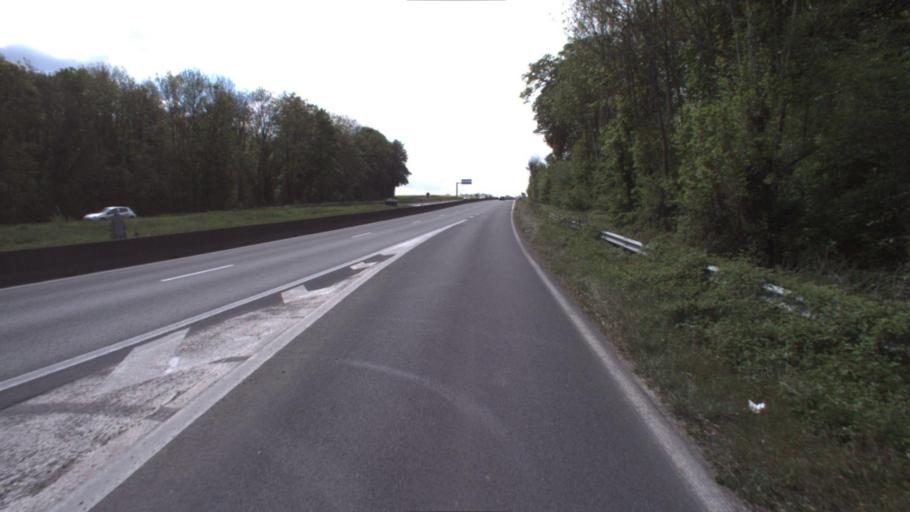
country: FR
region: Ile-de-France
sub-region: Departement de Seine-et-Marne
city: Tournan-en-Brie
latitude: 48.7369
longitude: 2.7585
